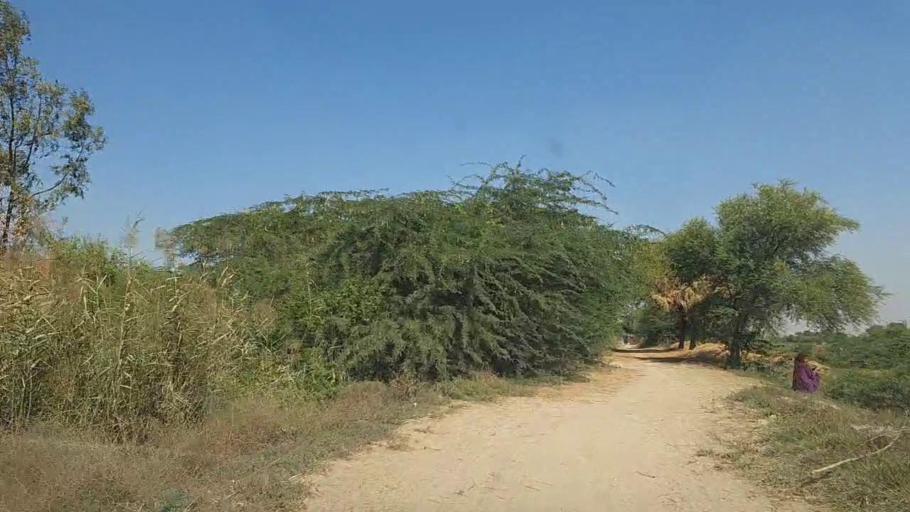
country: PK
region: Sindh
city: Thatta
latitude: 24.7842
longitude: 67.9731
